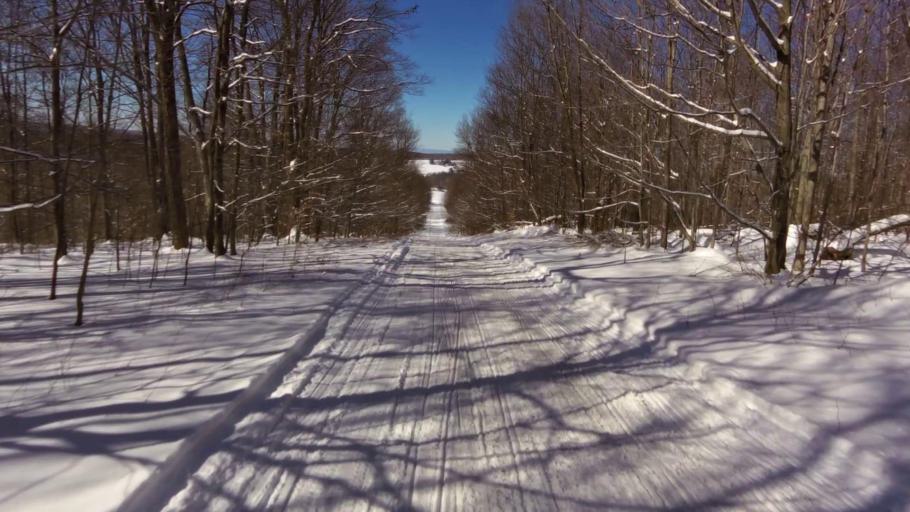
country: US
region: New York
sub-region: Chautauqua County
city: Mayville
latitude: 42.2461
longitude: -79.4195
